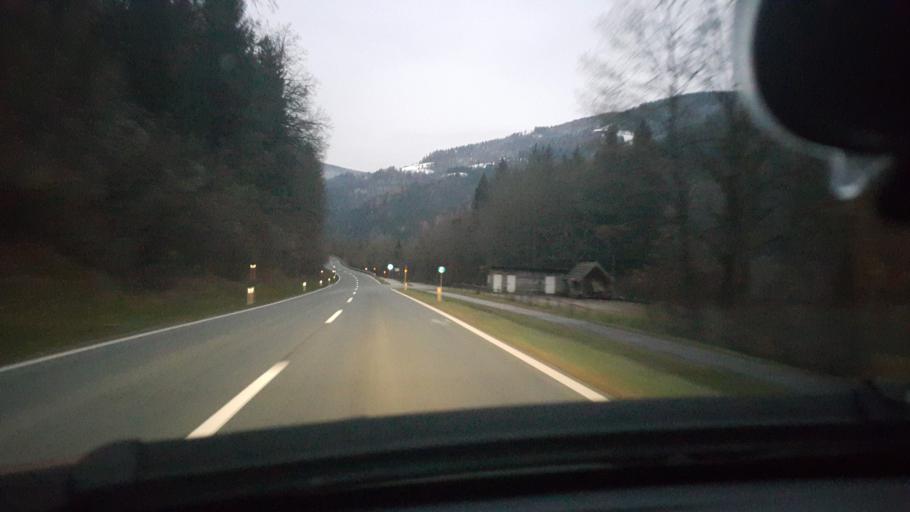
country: AT
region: Carinthia
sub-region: Politischer Bezirk Wolfsberg
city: Lavamund
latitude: 46.6134
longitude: 14.9757
